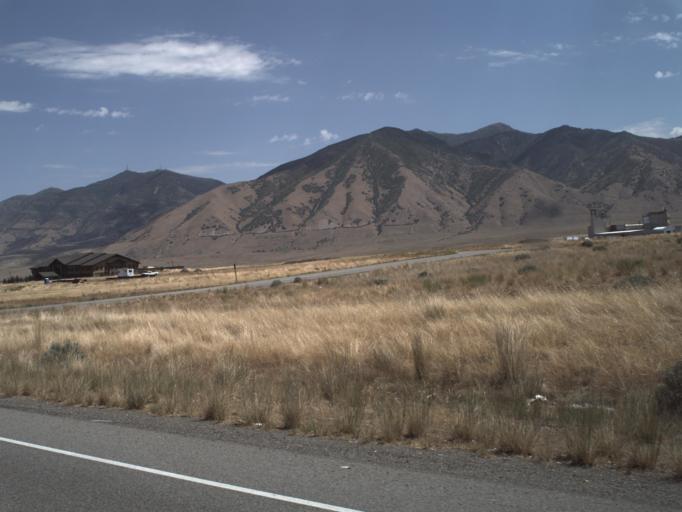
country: US
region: Utah
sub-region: Tooele County
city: Tooele
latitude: 40.5655
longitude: -112.2959
